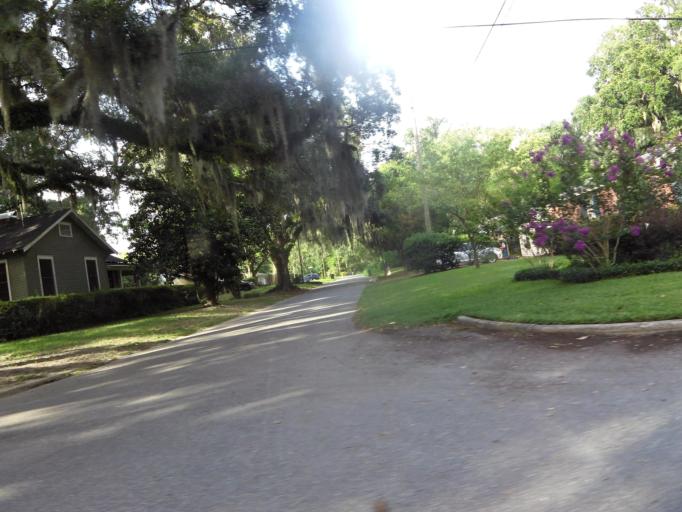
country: US
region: Florida
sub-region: Duval County
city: Jacksonville
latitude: 30.2714
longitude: -81.7077
